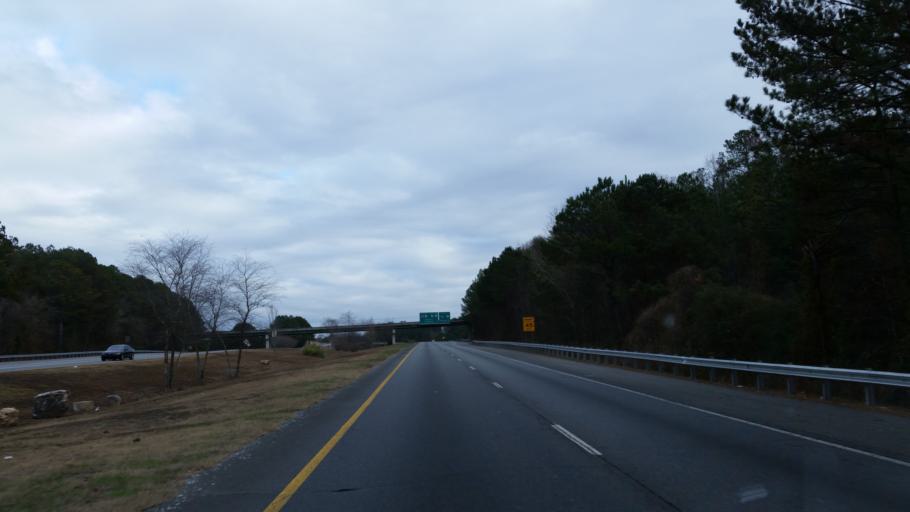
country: US
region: Georgia
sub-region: Cherokee County
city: Canton
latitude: 34.2205
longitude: -84.4945
